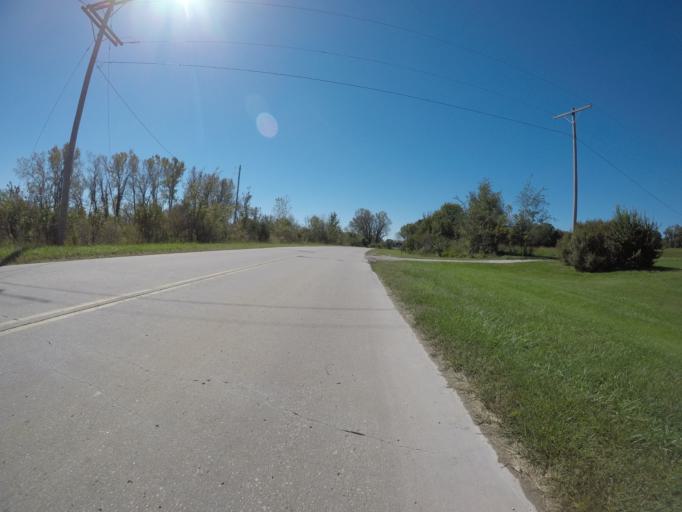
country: US
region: Kansas
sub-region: Wyandotte County
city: Bonner Springs
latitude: 39.0386
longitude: -94.8926
